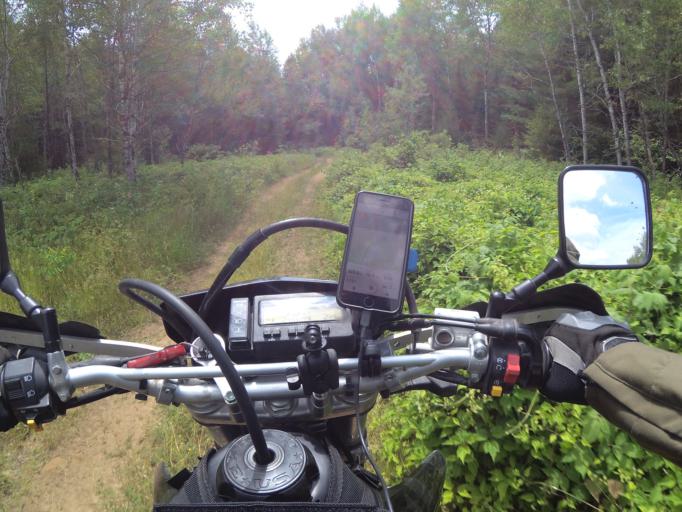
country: CA
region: Ontario
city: Bancroft
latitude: 45.0246
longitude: -77.2638
